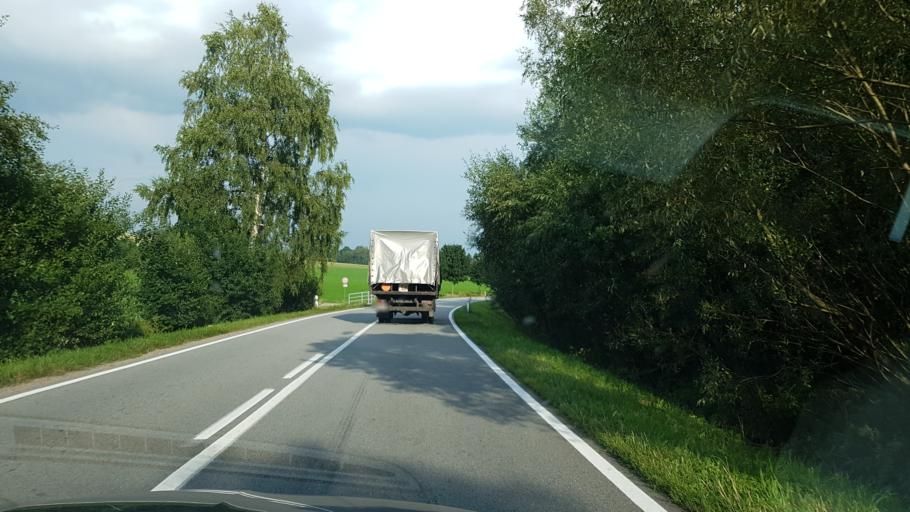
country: PL
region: Lower Silesian Voivodeship
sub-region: Powiat klodzki
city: Miedzylesie
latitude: 50.0988
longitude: 16.6515
